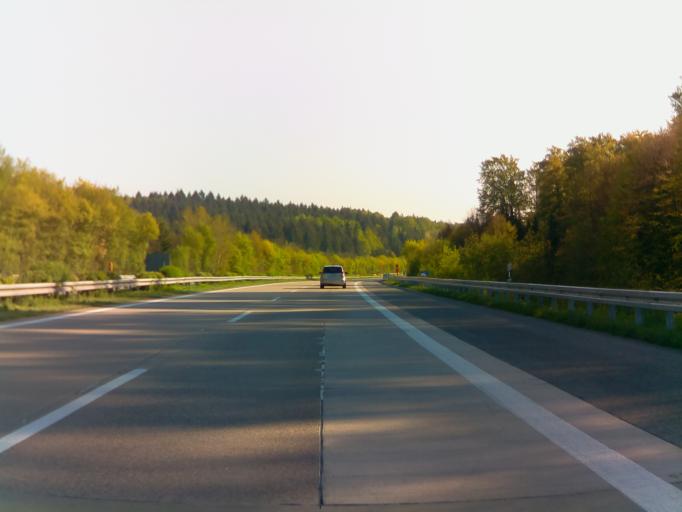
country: DE
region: Baden-Wuerttemberg
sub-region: Karlsruhe Region
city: Rosenberg
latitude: 49.4165
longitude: 9.4777
